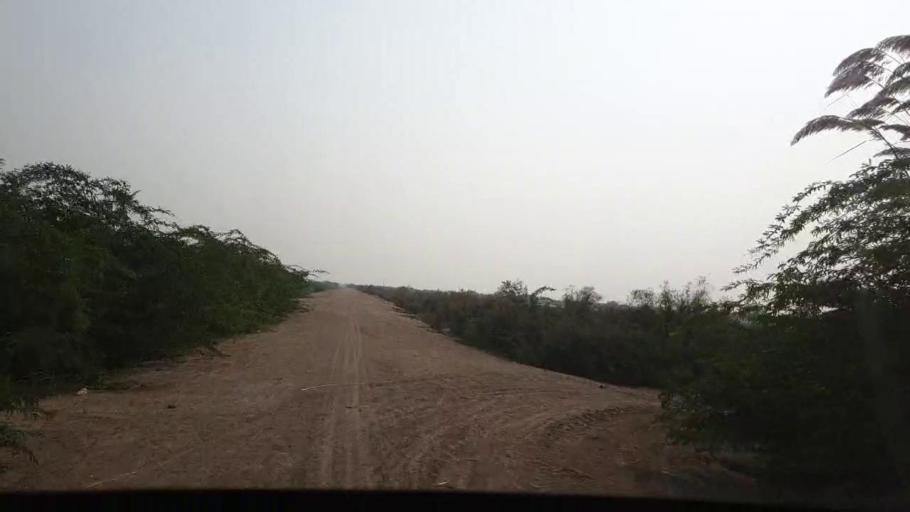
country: PK
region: Sindh
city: Jati
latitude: 24.2766
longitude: 68.4231
